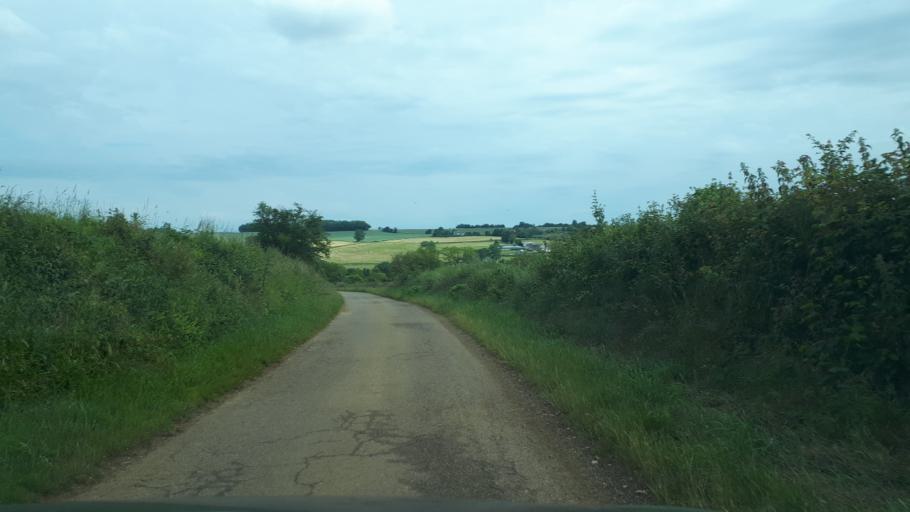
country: FR
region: Centre
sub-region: Departement du Cher
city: Sancerre
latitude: 47.3234
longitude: 2.7243
